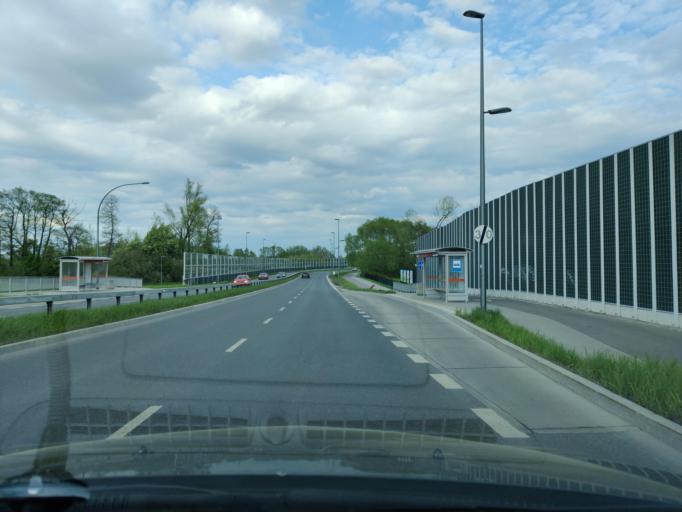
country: PL
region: Masovian Voivodeship
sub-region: Warszawa
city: Kabaty
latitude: 52.1304
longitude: 21.0839
